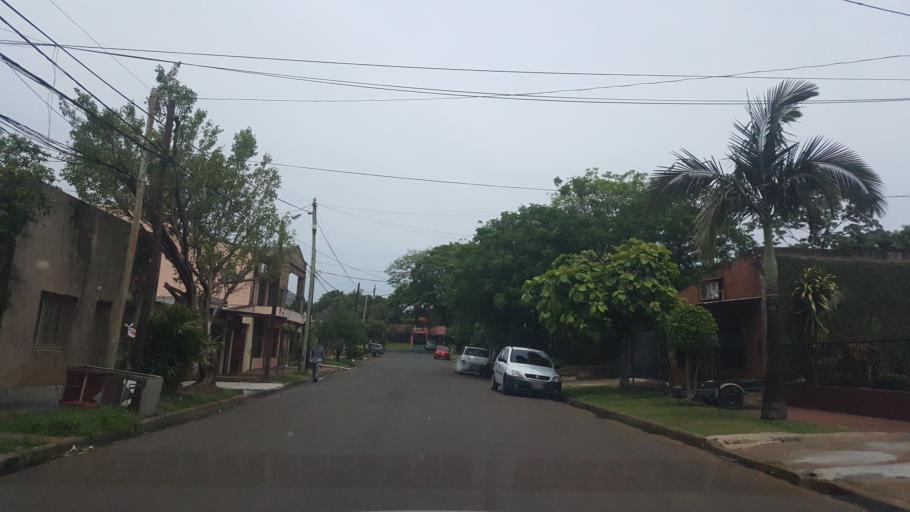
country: AR
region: Misiones
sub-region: Departamento de Capital
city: Posadas
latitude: -27.3678
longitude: -55.9148
